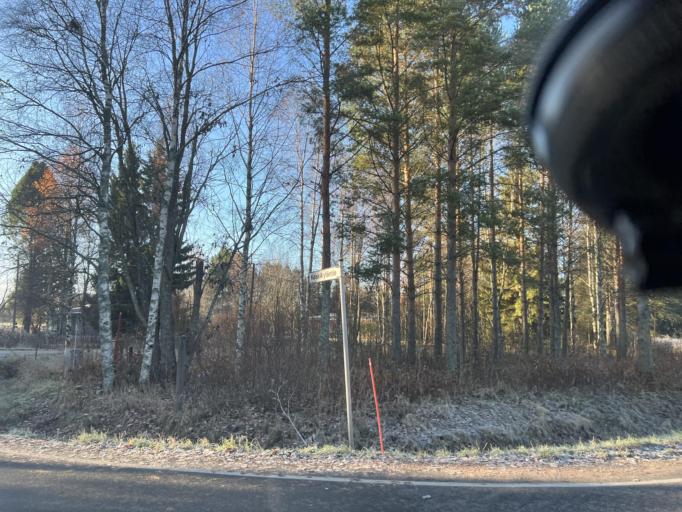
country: FI
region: Northern Ostrobothnia
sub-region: Oulu
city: Tyrnaevae
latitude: 64.7626
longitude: 25.6362
